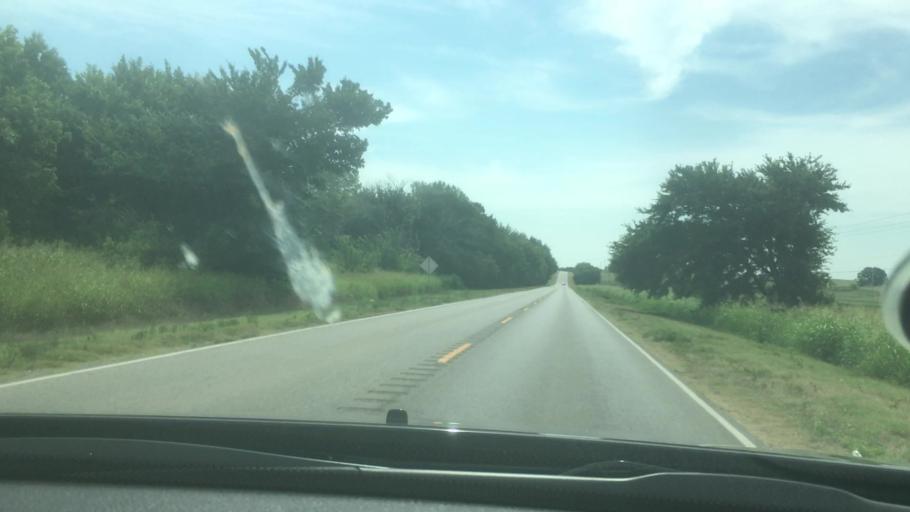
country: US
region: Oklahoma
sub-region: Garvin County
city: Maysville
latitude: 34.8147
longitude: -97.3911
